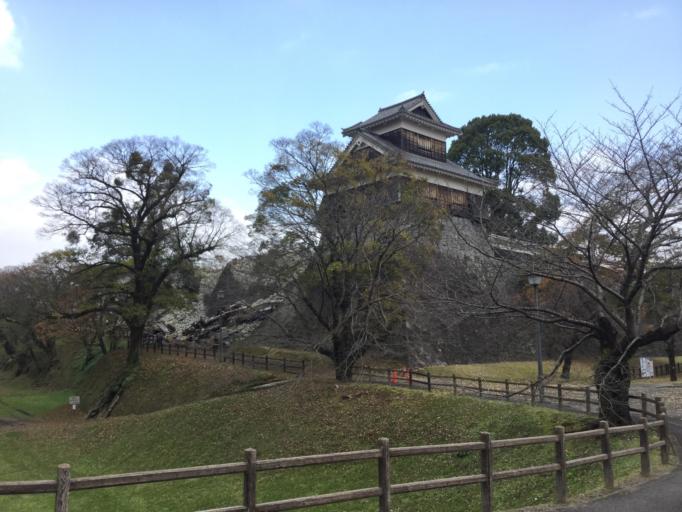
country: JP
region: Kumamoto
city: Kumamoto
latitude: 32.8044
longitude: 130.7028
